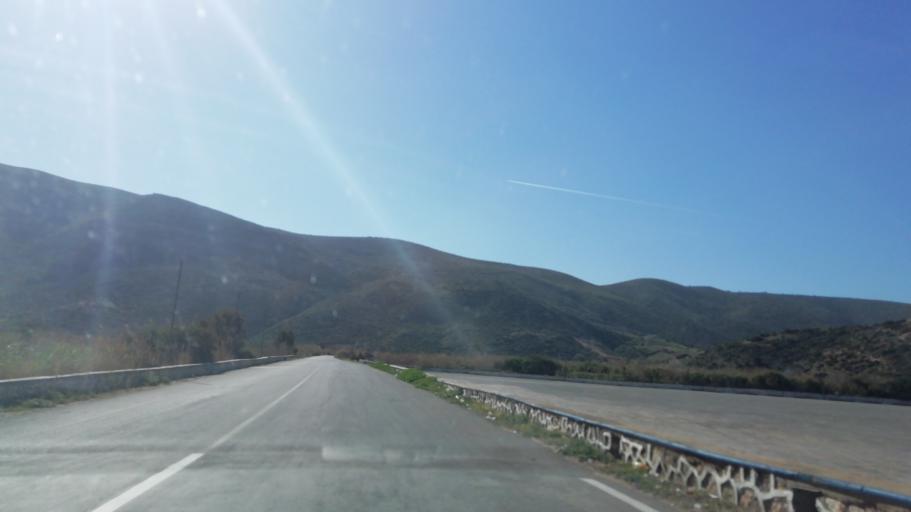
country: DZ
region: Ain Temouchent
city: El Amria
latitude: 35.6386
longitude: -1.0590
